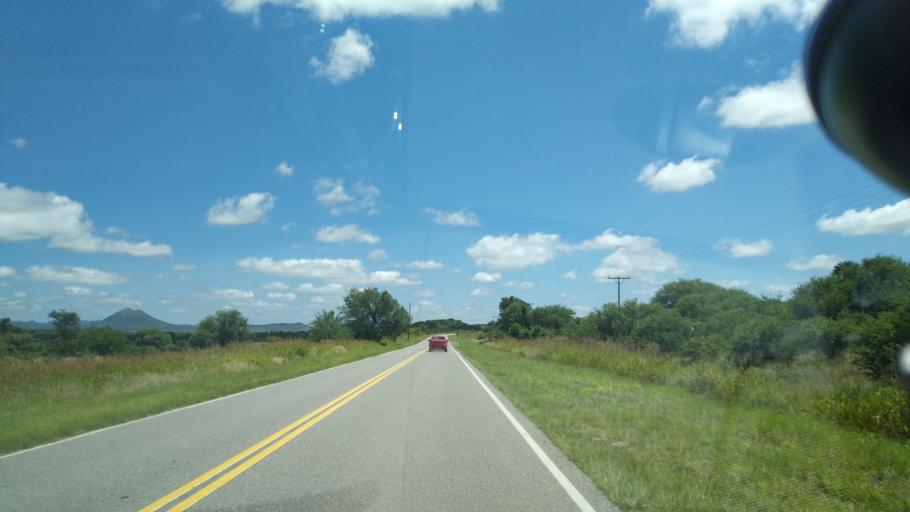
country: AR
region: Cordoba
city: Salsacate
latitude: -31.4135
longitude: -65.0956
